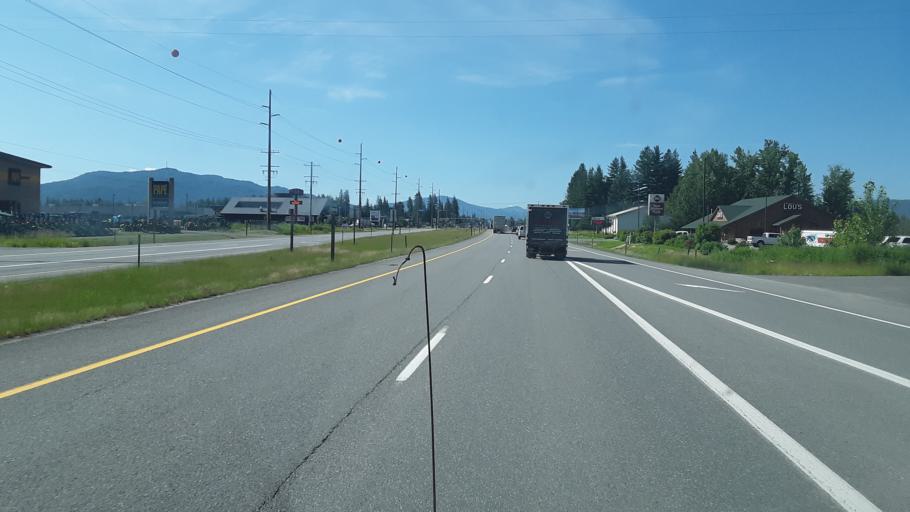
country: US
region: Idaho
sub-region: Bonner County
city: Ponderay
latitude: 48.3134
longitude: -116.5464
